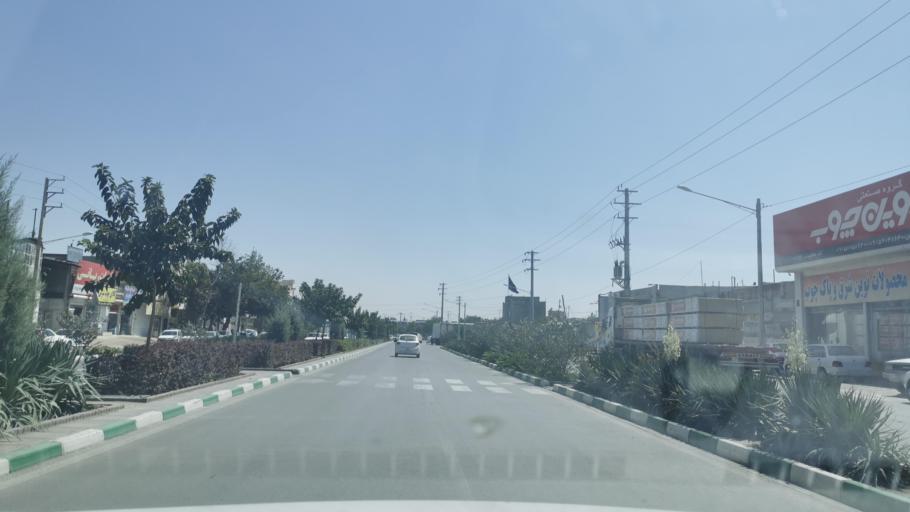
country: IR
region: Razavi Khorasan
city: Mashhad
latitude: 36.3517
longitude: 59.5736
